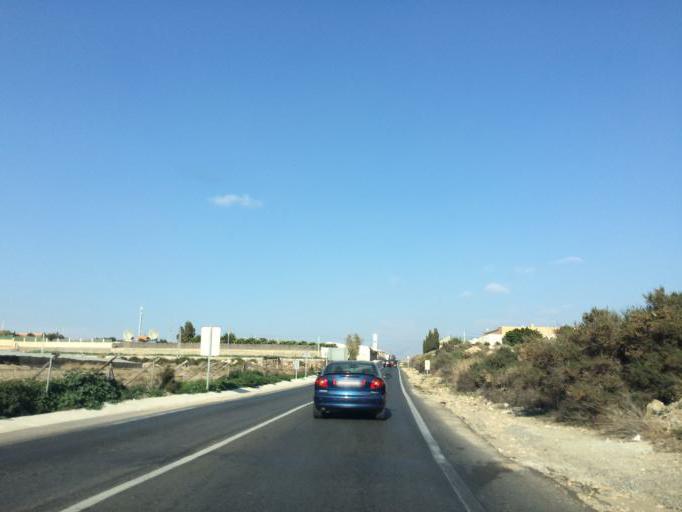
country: ES
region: Andalusia
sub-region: Provincia de Almeria
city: Huercal de Almeria
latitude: 36.8541
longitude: -2.4204
